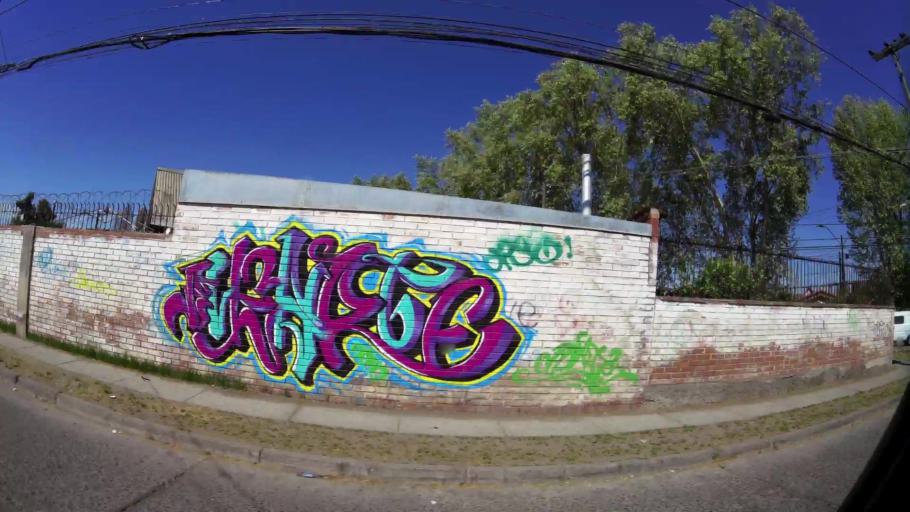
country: CL
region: Santiago Metropolitan
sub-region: Provincia de Talagante
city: Penaflor
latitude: -33.6047
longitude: -70.8890
